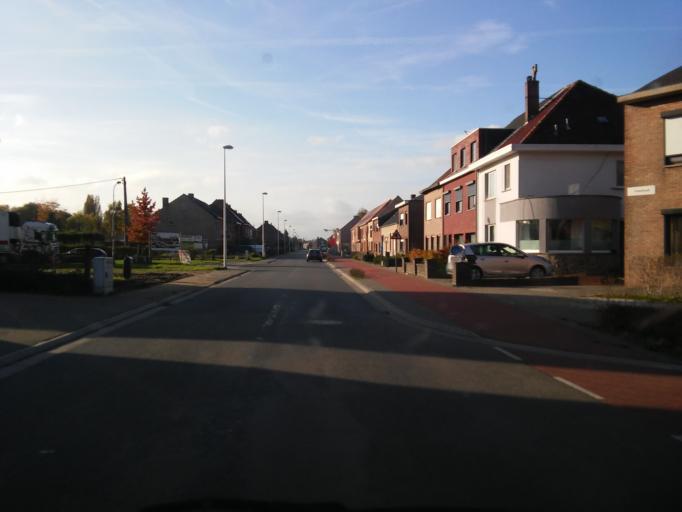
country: BE
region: Flanders
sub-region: Provincie Antwerpen
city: Duffel
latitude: 51.0929
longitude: 4.5253
